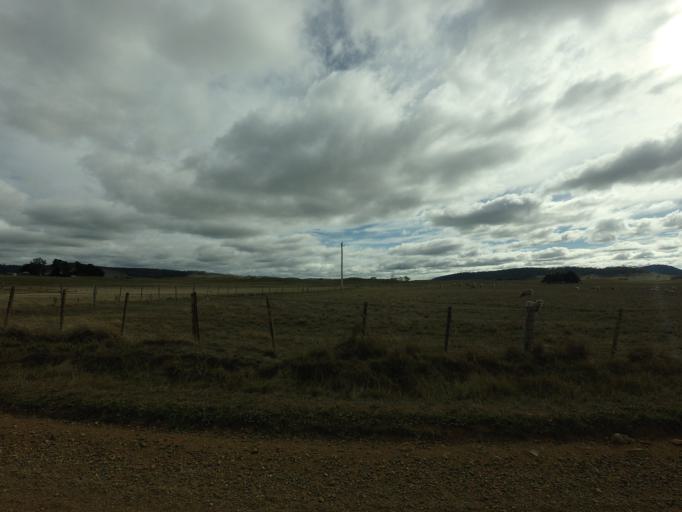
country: AU
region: Tasmania
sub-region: Brighton
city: Bridgewater
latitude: -42.4256
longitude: 147.3899
